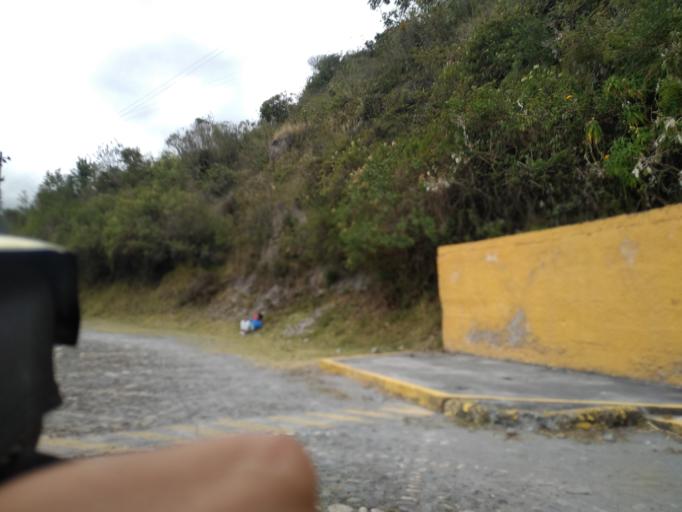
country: EC
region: Imbabura
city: Cotacachi
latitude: 0.2923
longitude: -78.3574
